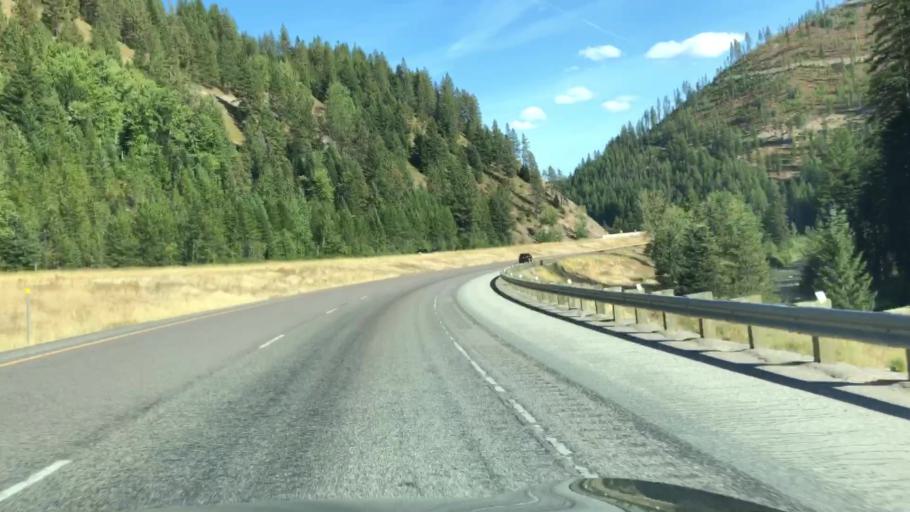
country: US
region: Montana
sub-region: Sanders County
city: Thompson Falls
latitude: 47.4038
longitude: -115.4771
